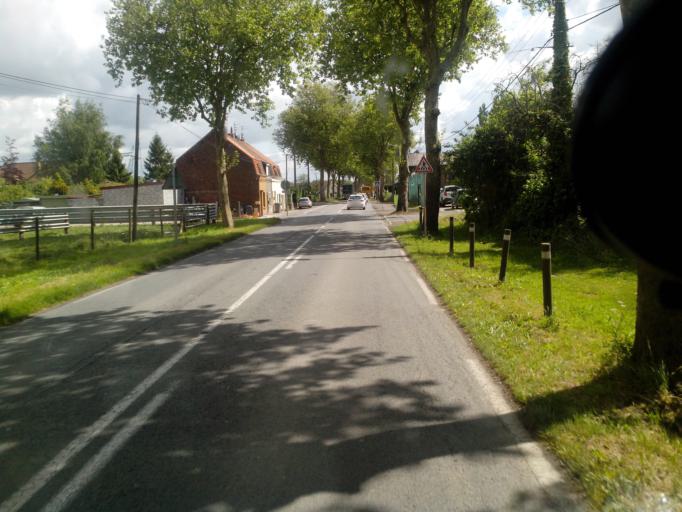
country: FR
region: Nord-Pas-de-Calais
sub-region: Departement du Pas-de-Calais
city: Fleurbaix
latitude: 50.6701
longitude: 2.8152
